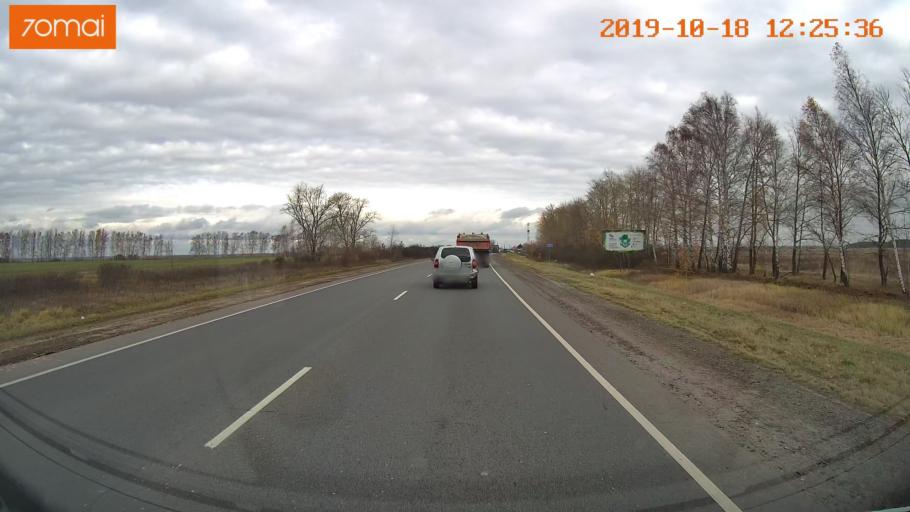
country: RU
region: Rjazan
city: Rybnoye
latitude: 54.5515
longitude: 39.5225
